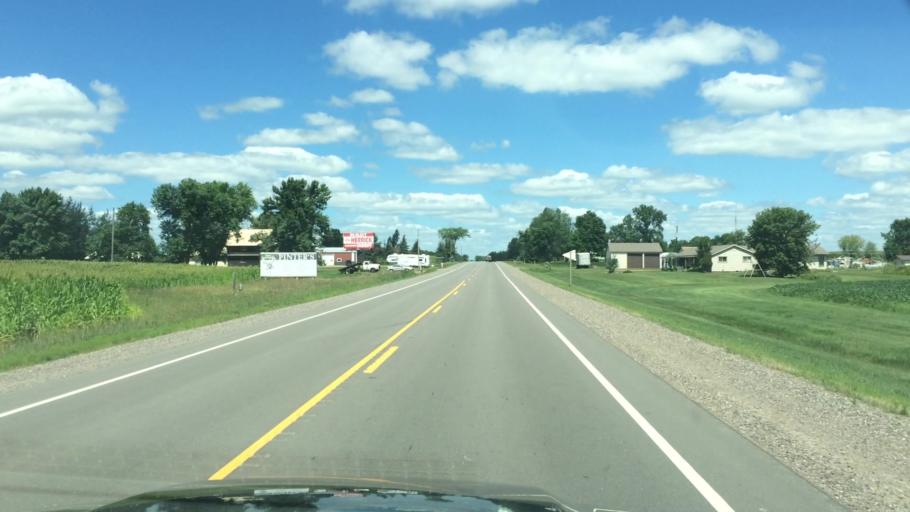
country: US
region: Wisconsin
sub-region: Clark County
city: Abbotsford
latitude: 45.0082
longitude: -90.3155
